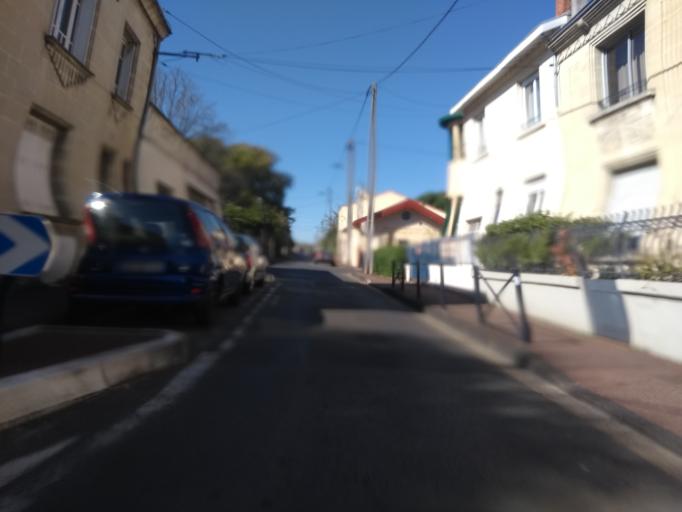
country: FR
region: Aquitaine
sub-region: Departement de la Gironde
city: Bordeaux
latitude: 44.8327
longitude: -0.6034
